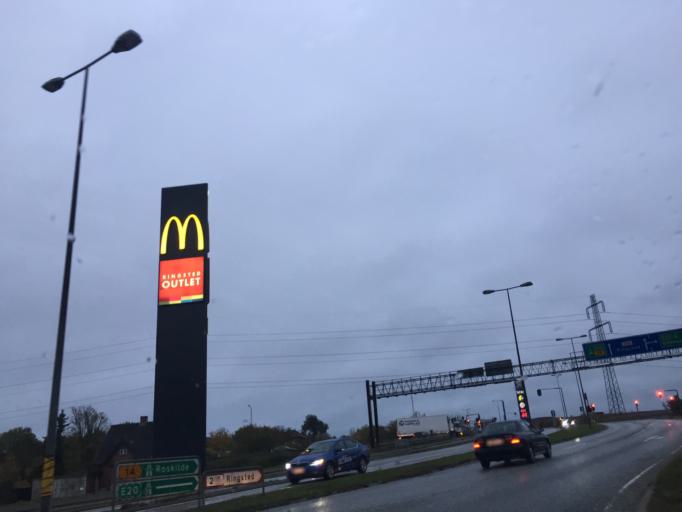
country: DK
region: Zealand
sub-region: Ringsted Kommune
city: Ringsted
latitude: 55.4568
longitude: 11.7914
